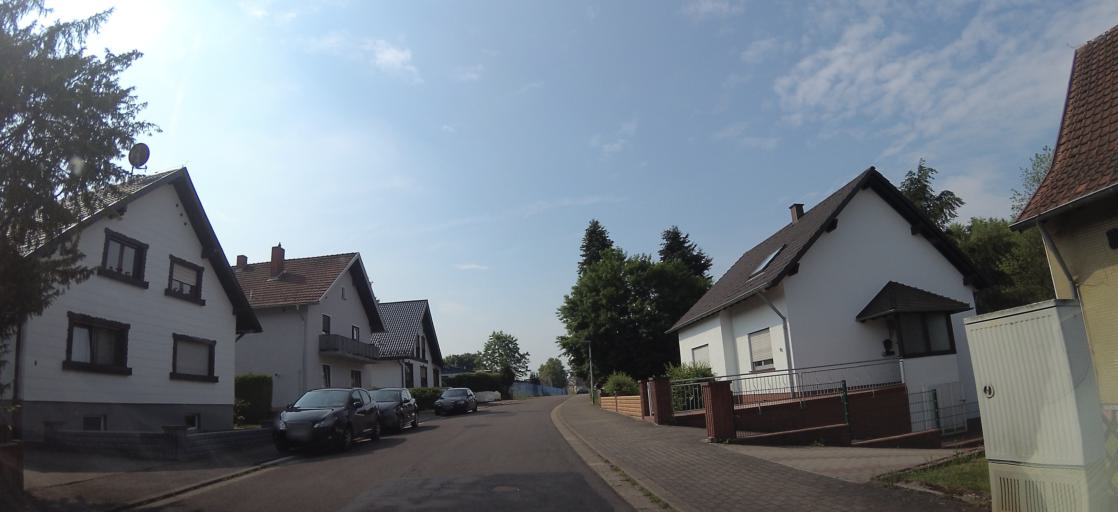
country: DE
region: Saarland
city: Bexbach
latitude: 49.3512
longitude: 7.2732
